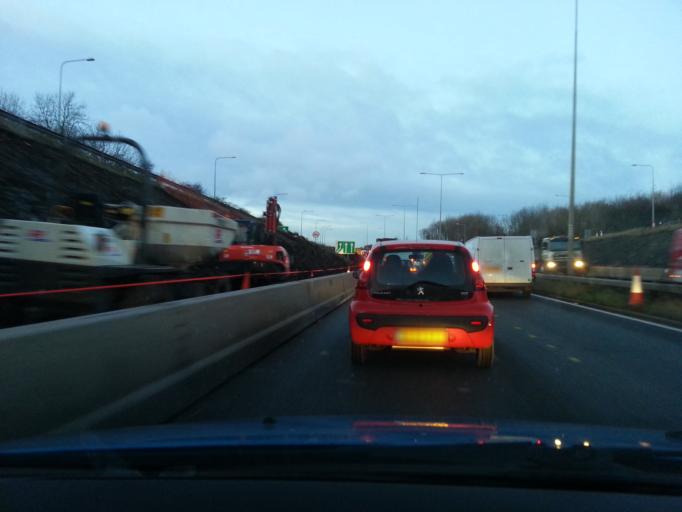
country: GB
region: England
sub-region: Gateshead
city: Lamesley
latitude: 54.9414
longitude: -1.6309
